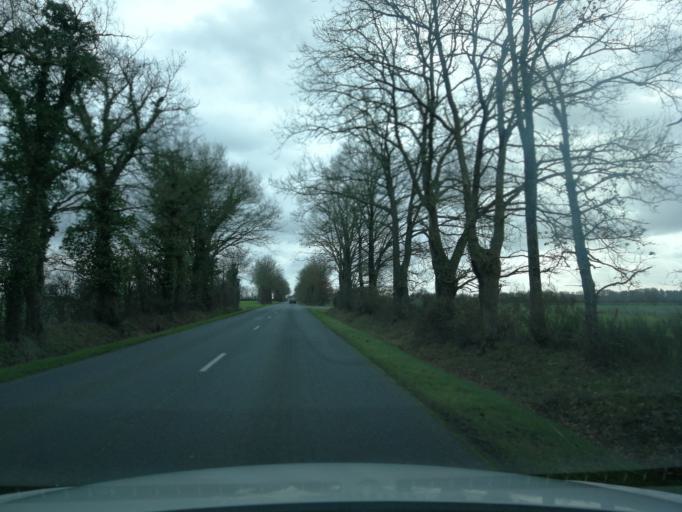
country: FR
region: Pays de la Loire
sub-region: Departement de la Loire-Atlantique
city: La Planche
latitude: 47.0083
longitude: -1.4758
